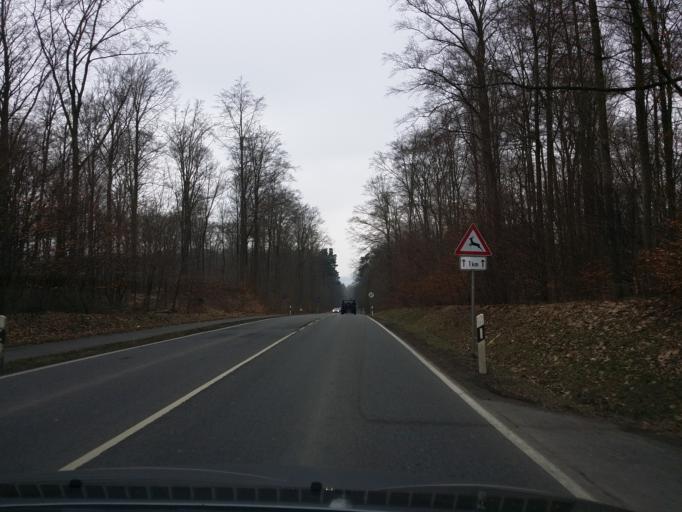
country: DE
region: Hesse
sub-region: Regierungsbezirk Darmstadt
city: Waldems
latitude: 50.2396
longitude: 8.2981
